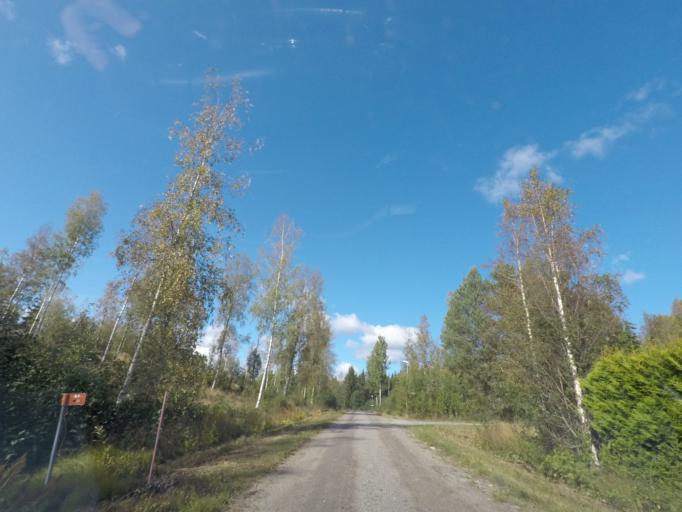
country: SE
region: Vaestmanland
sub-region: Skinnskattebergs Kommun
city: Skinnskatteberg
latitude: 59.8299
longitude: 15.5210
